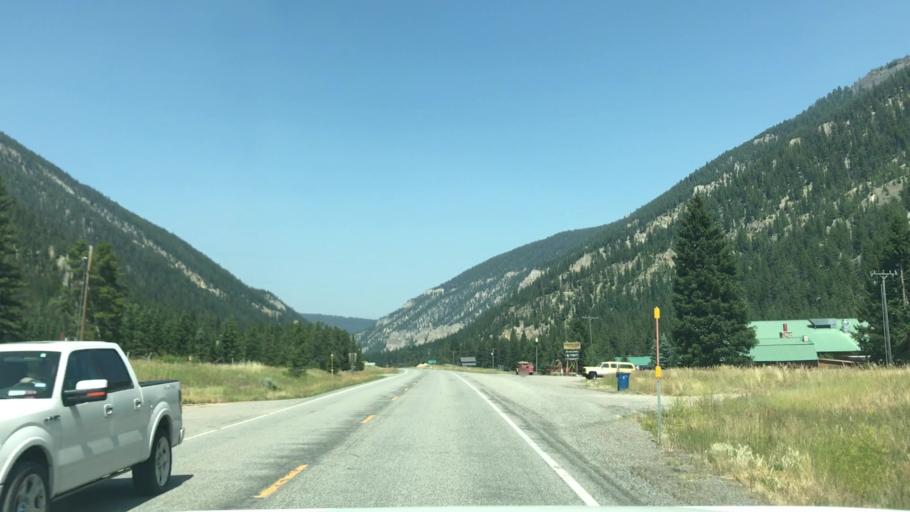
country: US
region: Montana
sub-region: Gallatin County
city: Big Sky
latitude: 45.1152
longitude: -111.2252
